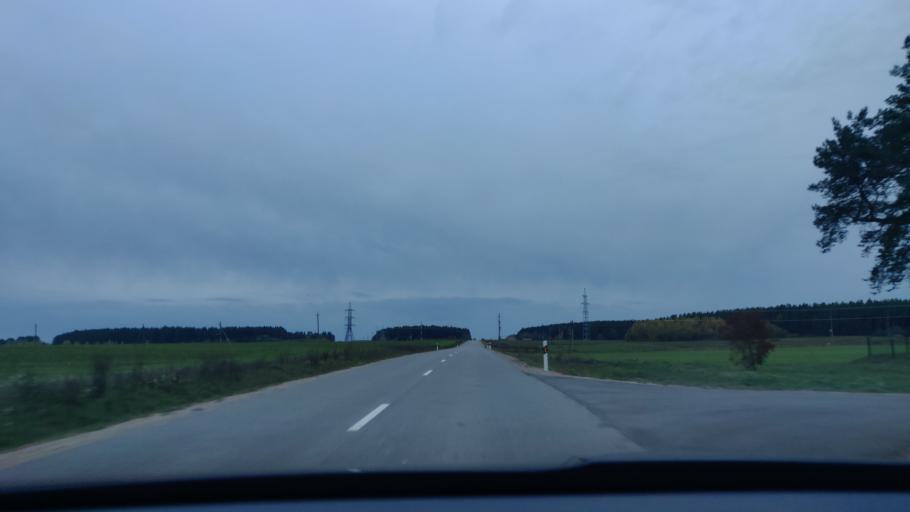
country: LT
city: Lentvaris
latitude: 54.5937
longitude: 25.0429
